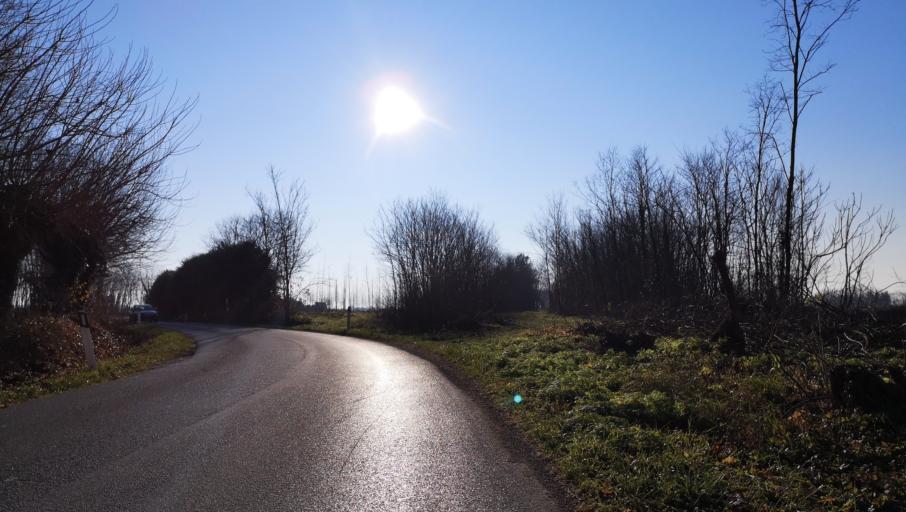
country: IT
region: Friuli Venezia Giulia
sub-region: Provincia di Udine
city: Bicinicco
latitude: 45.9519
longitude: 13.2692
